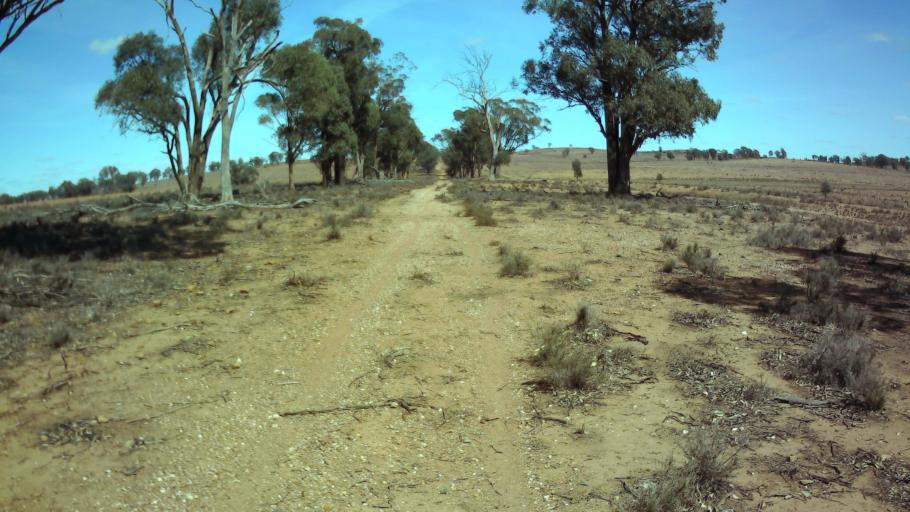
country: AU
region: New South Wales
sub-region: Weddin
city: Grenfell
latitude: -33.7217
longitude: 147.8473
